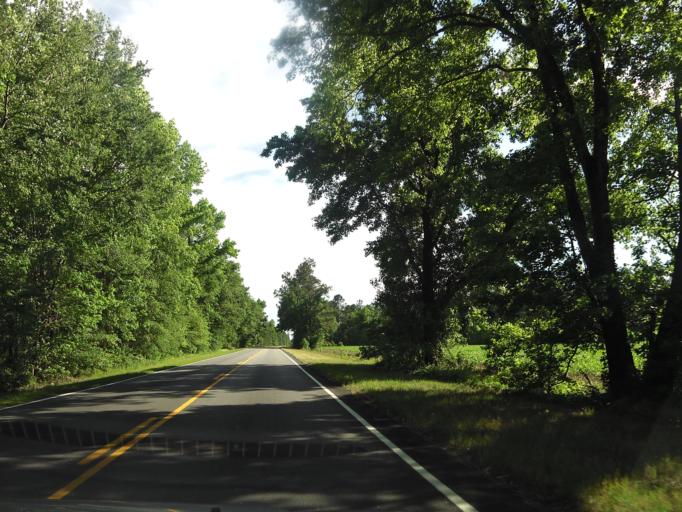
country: US
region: South Carolina
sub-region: Allendale County
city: Fairfax
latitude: 33.0013
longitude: -81.2199
